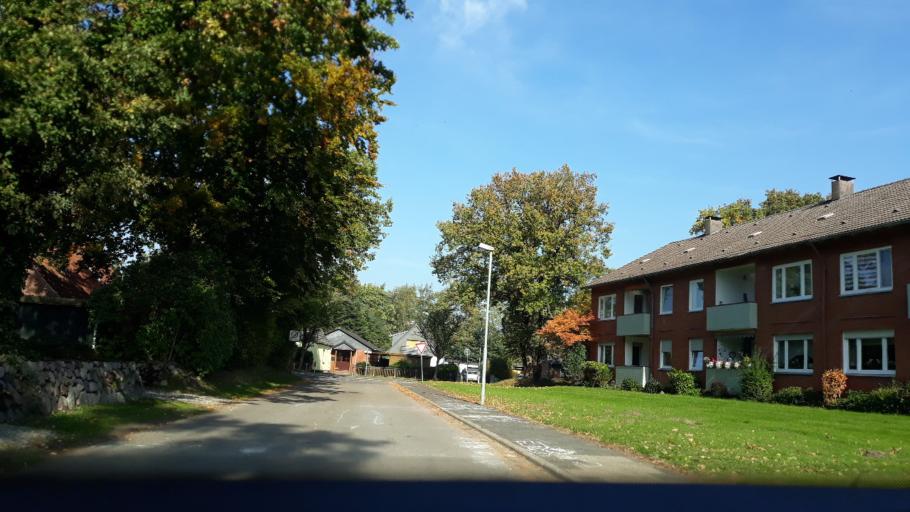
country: DE
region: Schleswig-Holstein
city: Kropp
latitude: 54.4149
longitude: 9.5178
